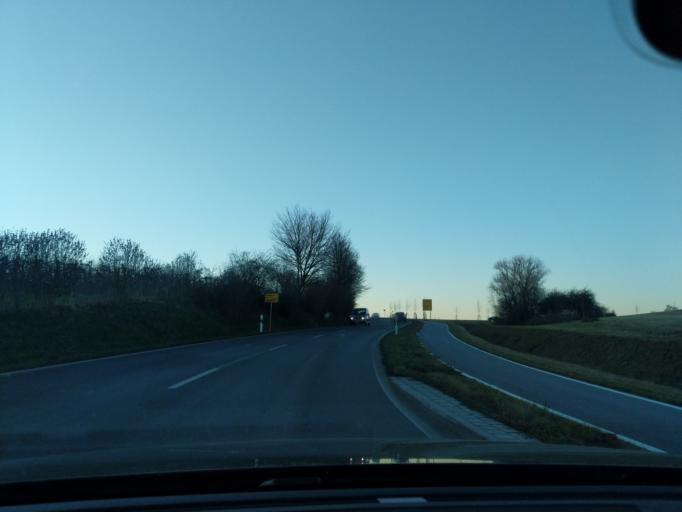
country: DE
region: Baden-Wuerttemberg
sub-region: Tuebingen Region
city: Bermatingen
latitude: 47.7279
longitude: 9.3168
